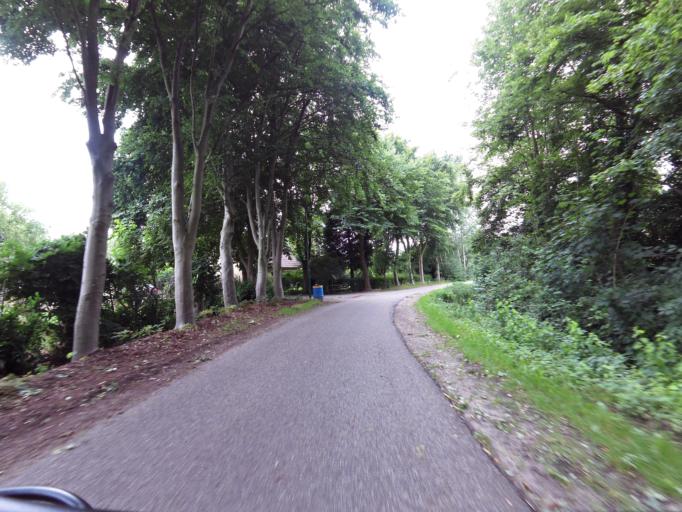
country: NL
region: North Brabant
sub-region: Gemeente Son en Breugel
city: Breugel
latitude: 51.5348
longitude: 5.5104
